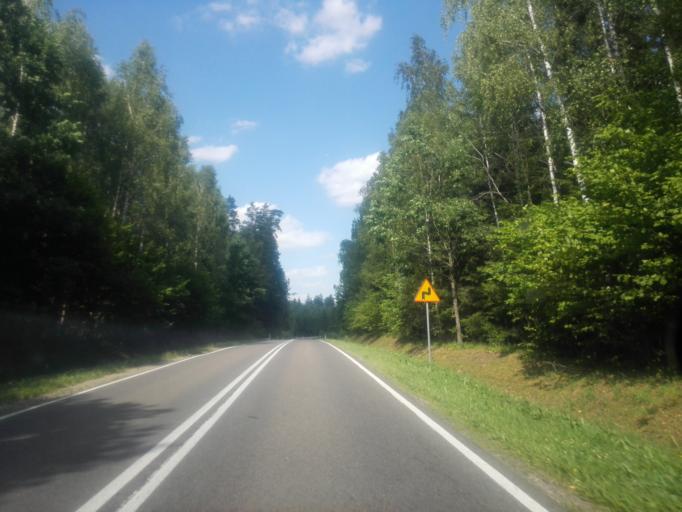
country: PL
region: Podlasie
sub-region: Powiat sejnenski
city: Sejny
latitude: 54.0069
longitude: 23.3224
